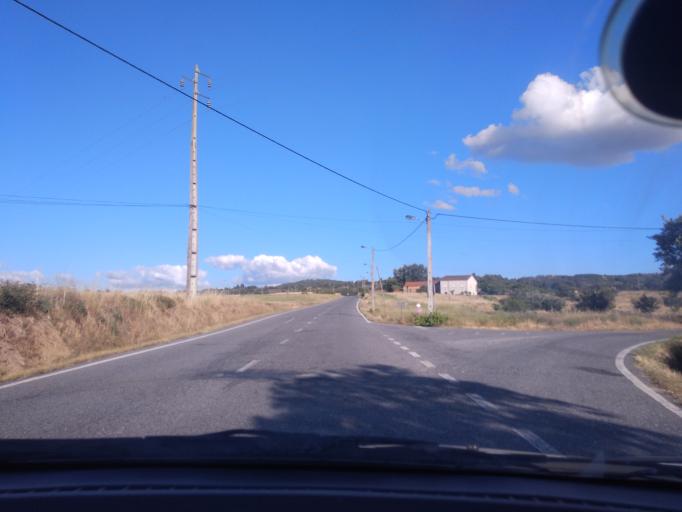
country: PT
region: Castelo Branco
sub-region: Covilha
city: Teixoso
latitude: 40.2511
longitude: -7.3987
